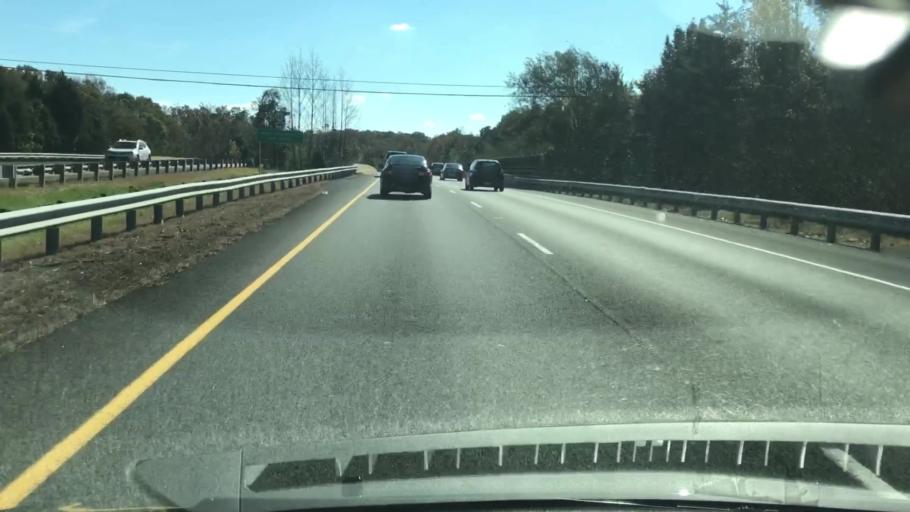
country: US
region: Virginia
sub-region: Fairfax County
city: Fairfax Station
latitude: 38.7999
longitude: -77.3408
